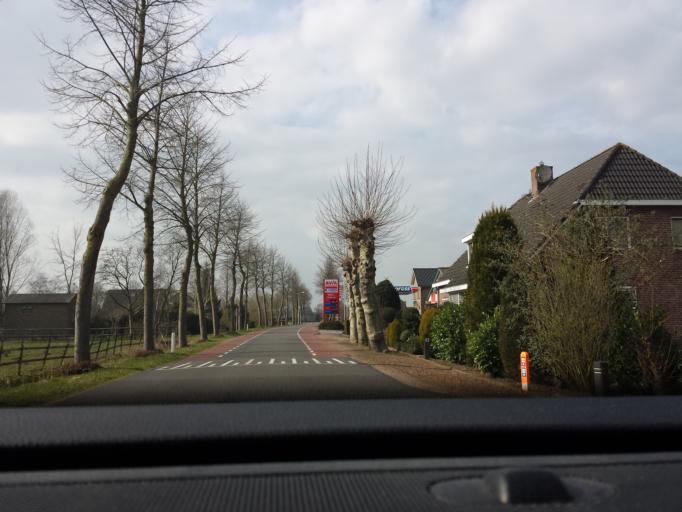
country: NL
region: Gelderland
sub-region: Oost Gelre
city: Lichtenvoorde
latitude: 52.0105
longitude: 6.5129
